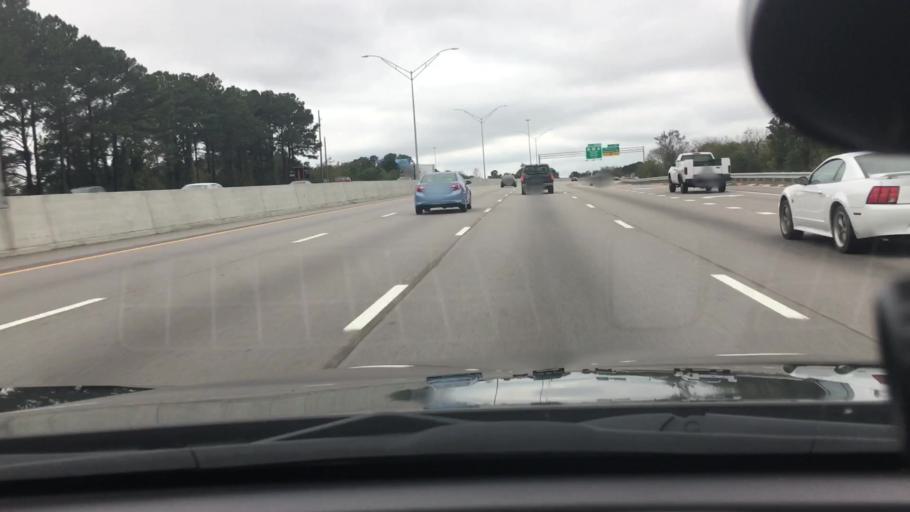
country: US
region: North Carolina
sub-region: Wake County
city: Raleigh
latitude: 35.7529
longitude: -78.6291
